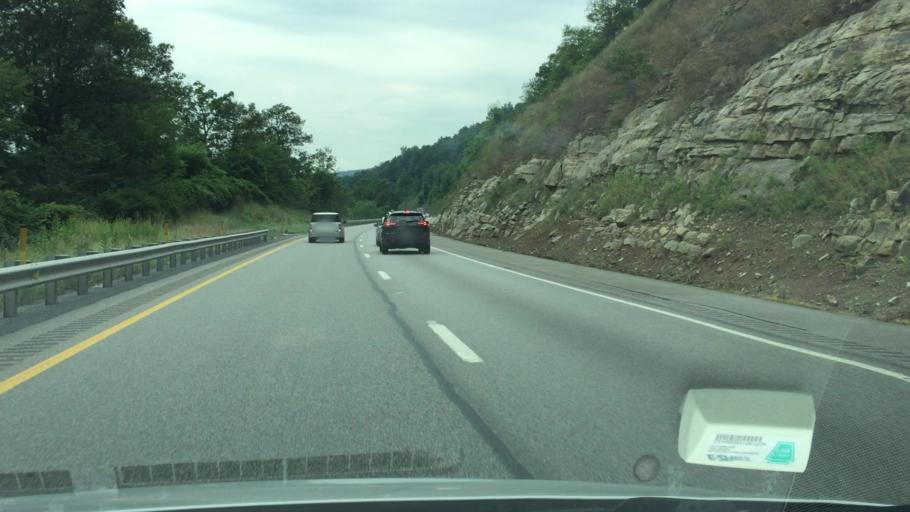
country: US
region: Pennsylvania
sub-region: Bedford County
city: Earlston
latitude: 39.8706
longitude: -78.2548
